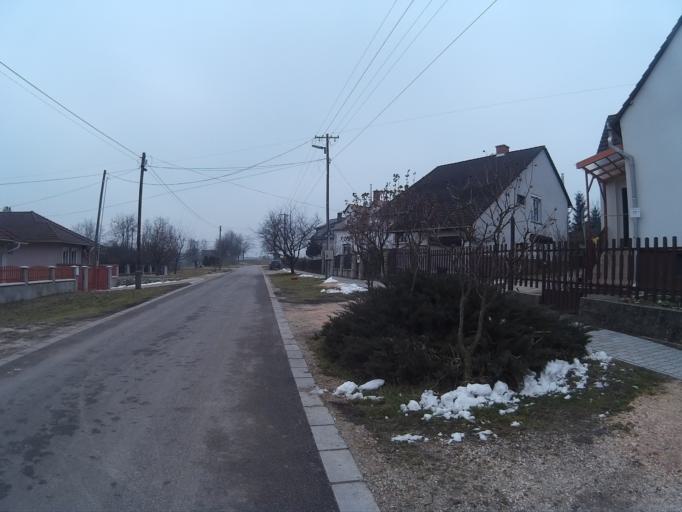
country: HU
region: Komarom-Esztergom
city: Tarjan
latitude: 47.6045
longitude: 18.5175
